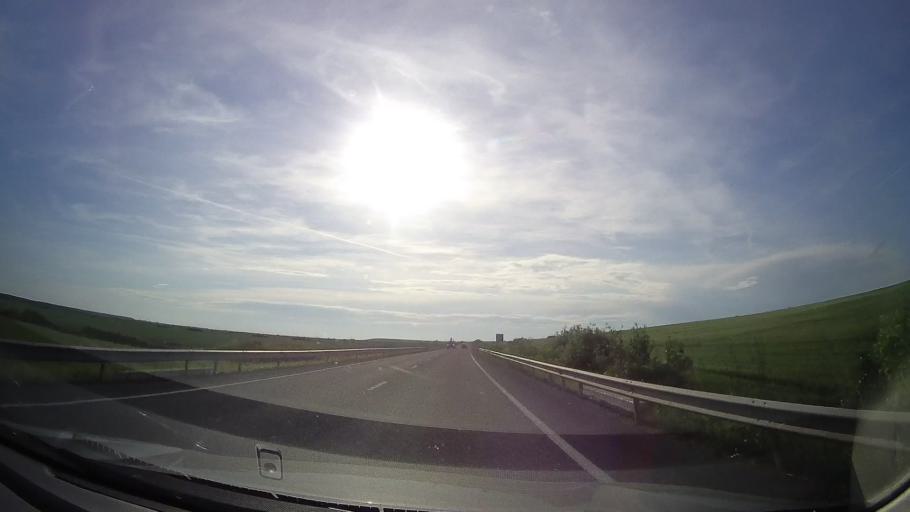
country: RO
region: Timis
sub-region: Comuna Topolovatu Mare
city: Topolovatu Mare
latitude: 45.7916
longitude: 21.5678
